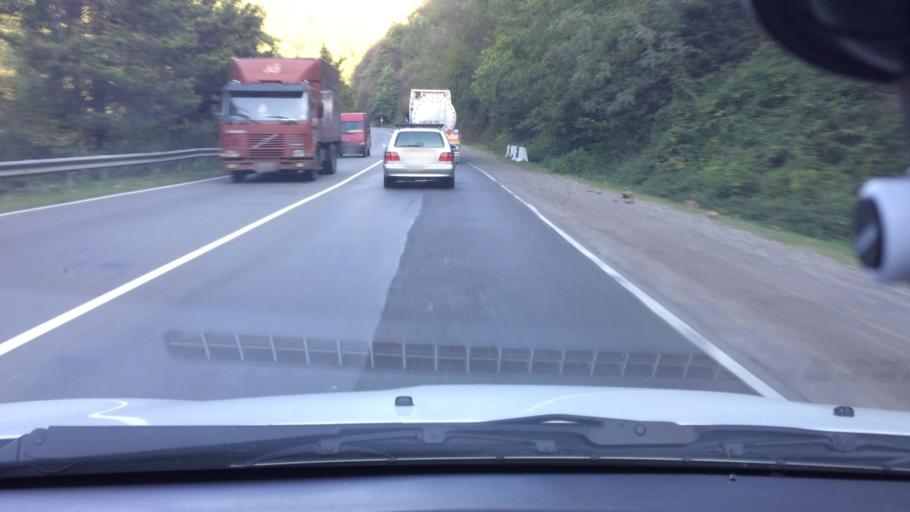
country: GE
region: Imereti
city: Kharagauli
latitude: 42.1052
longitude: 43.2060
